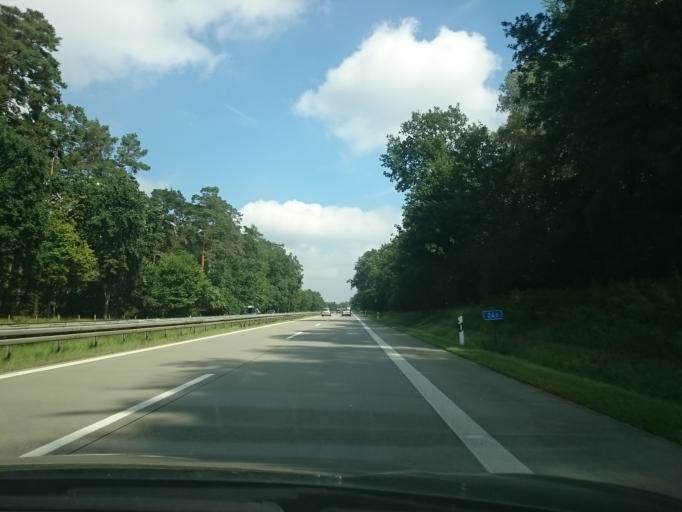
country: DE
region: Brandenburg
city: Marienwerder
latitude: 52.8073
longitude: 13.6233
